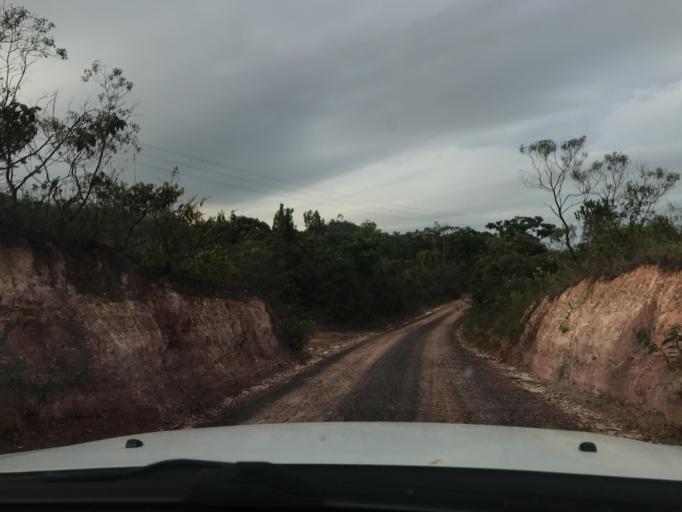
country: BR
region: Bahia
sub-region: Entre Rios
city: Entre Rios
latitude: -12.0529
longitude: -38.2277
